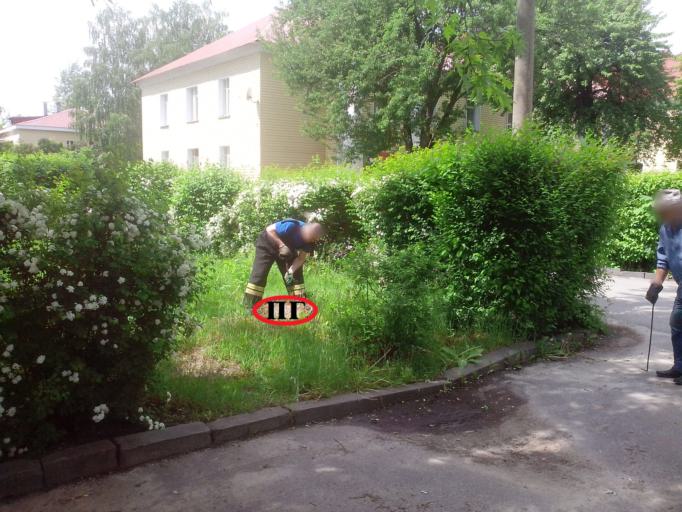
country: RU
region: Voronezj
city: Voronezh
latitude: 51.6244
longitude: 39.1928
